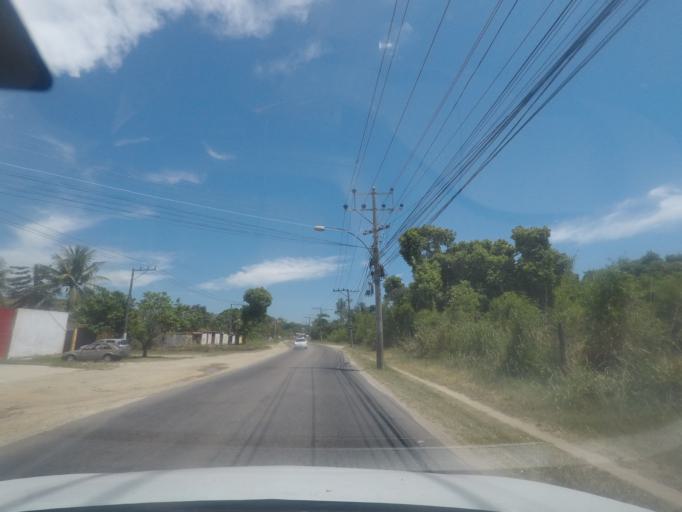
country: BR
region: Rio de Janeiro
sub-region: Itaguai
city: Itaguai
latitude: -22.9905
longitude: -43.6515
